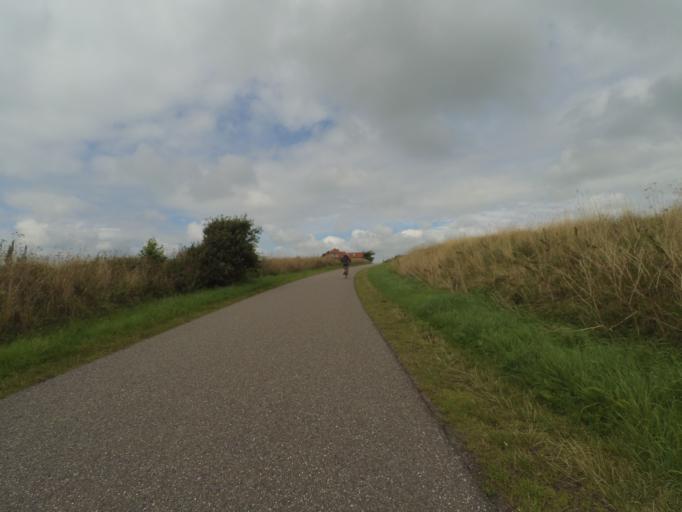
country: NL
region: North Holland
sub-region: Gemeente Texel
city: Den Burg
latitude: 53.0412
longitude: 4.8183
